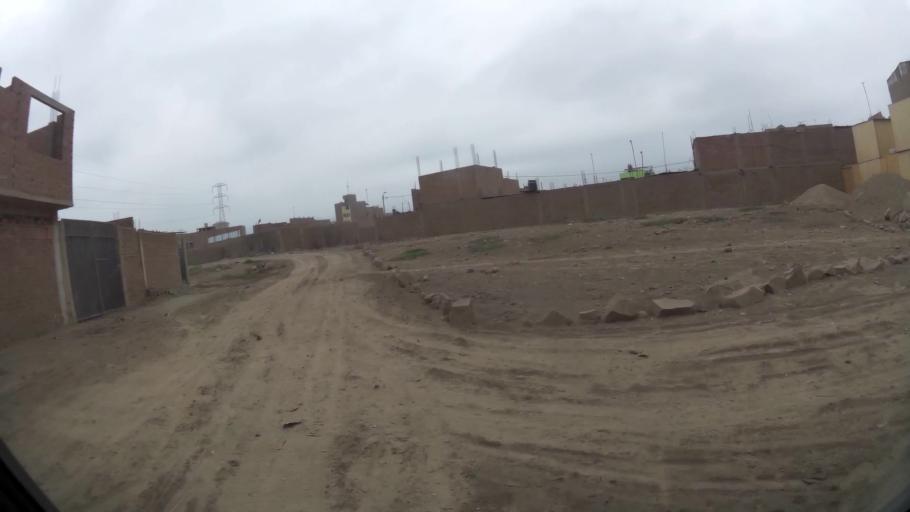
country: PE
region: Lima
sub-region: Lima
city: Independencia
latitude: -11.9557
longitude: -77.0967
